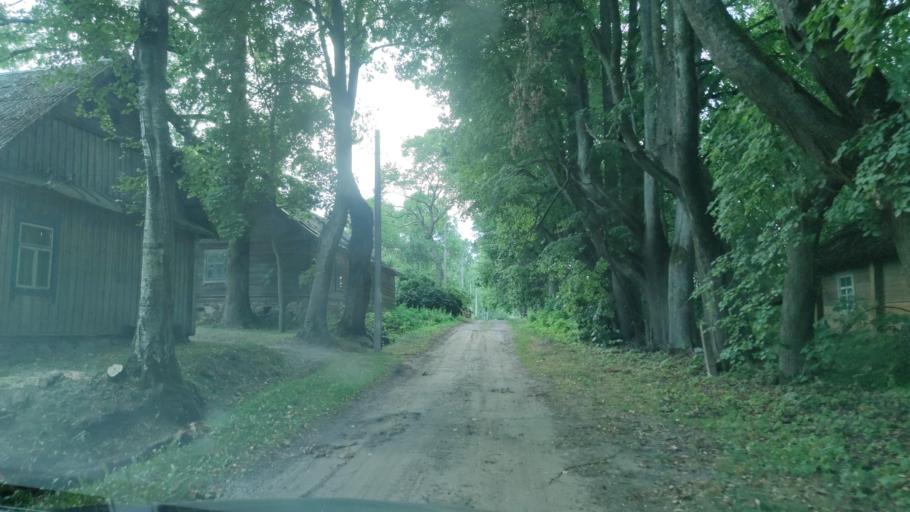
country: BY
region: Vitebsk
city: Mosar
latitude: 55.1236
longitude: 27.1764
